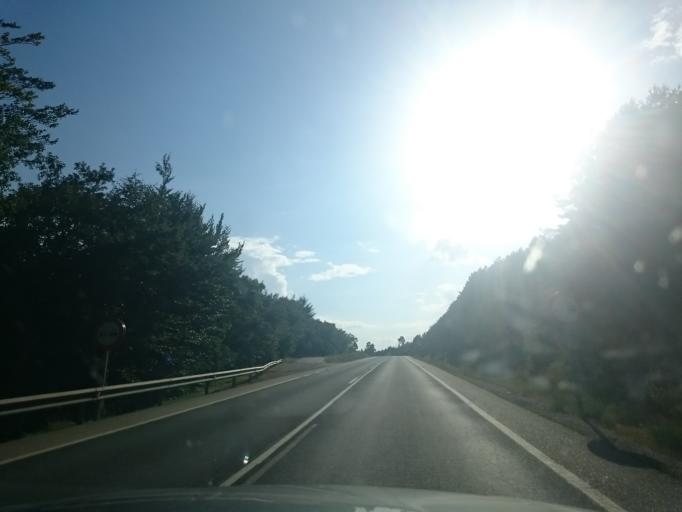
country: ES
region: Castille and Leon
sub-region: Provincia de Burgos
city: Cerraton de Juarros
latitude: 42.3736
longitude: -3.3368
